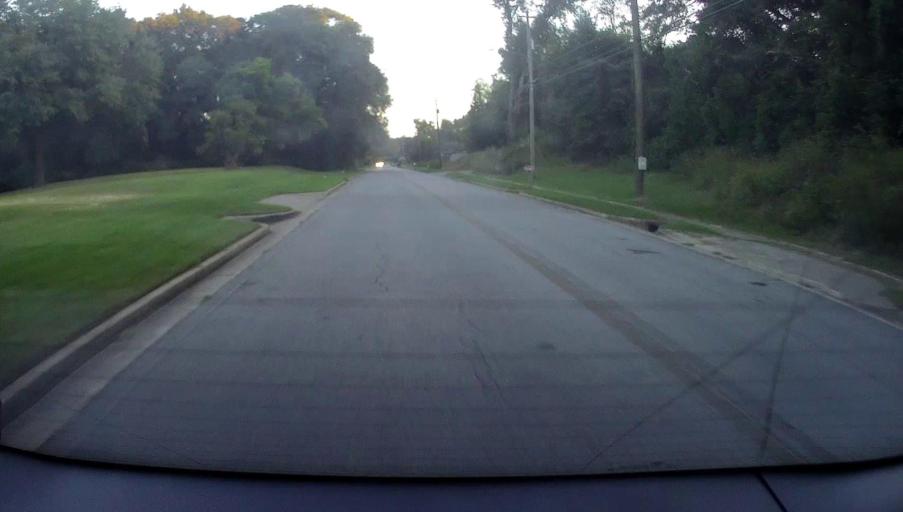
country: US
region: Georgia
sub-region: Houston County
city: Perry
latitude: 32.4541
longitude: -83.7398
